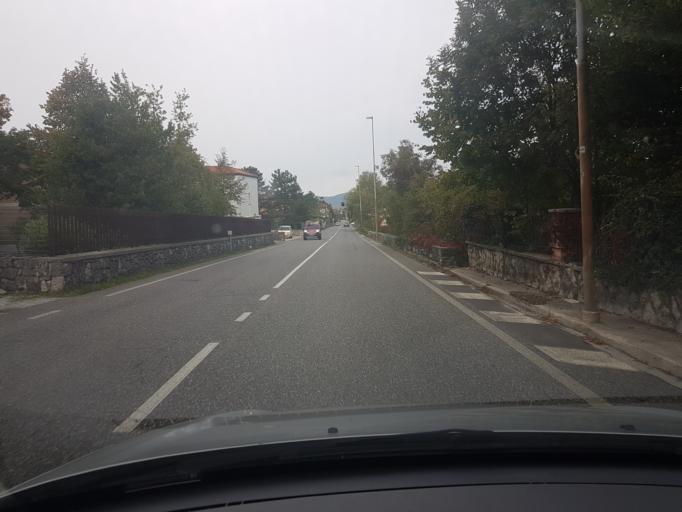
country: IT
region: Friuli Venezia Giulia
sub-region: Provincia di Trieste
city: Aurisina
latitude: 45.7464
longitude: 13.6765
